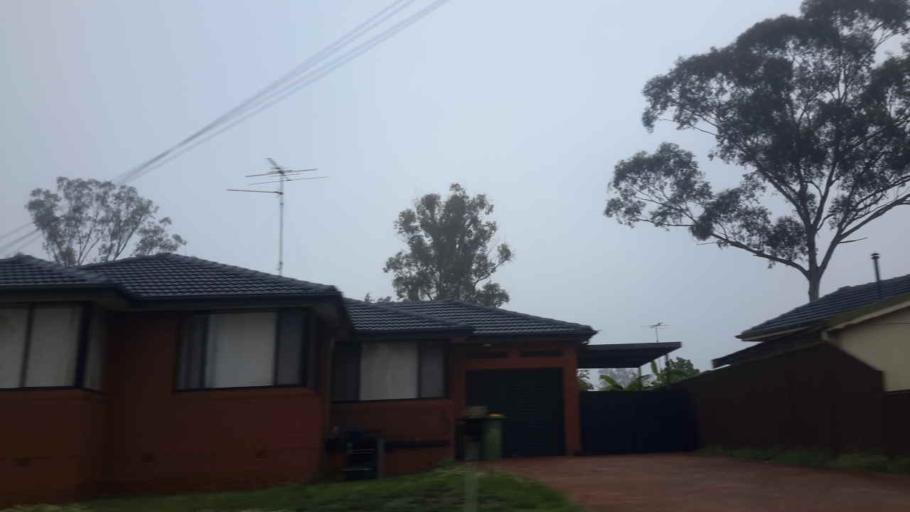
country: AU
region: New South Wales
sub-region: Penrith Municipality
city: Cambridge Park
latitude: -33.7446
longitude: 150.7148
